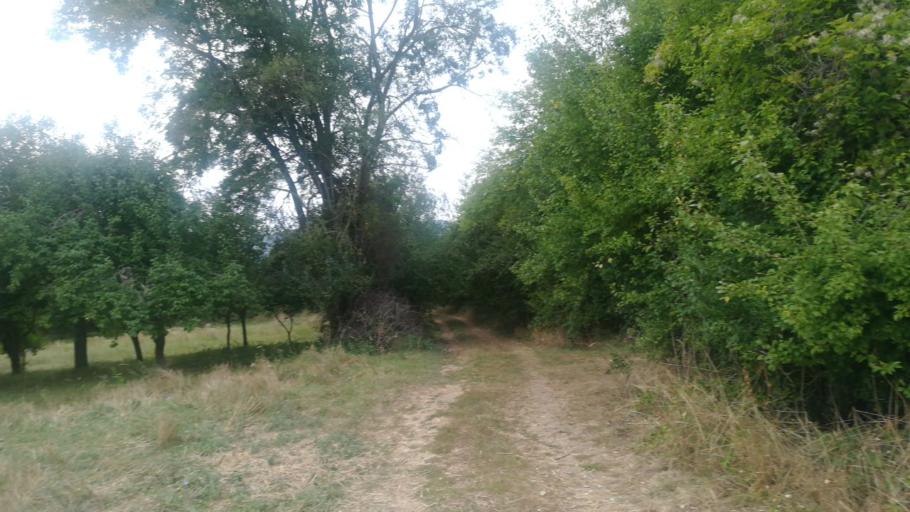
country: MK
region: Debarca
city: Belcista
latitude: 41.2855
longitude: 20.8288
